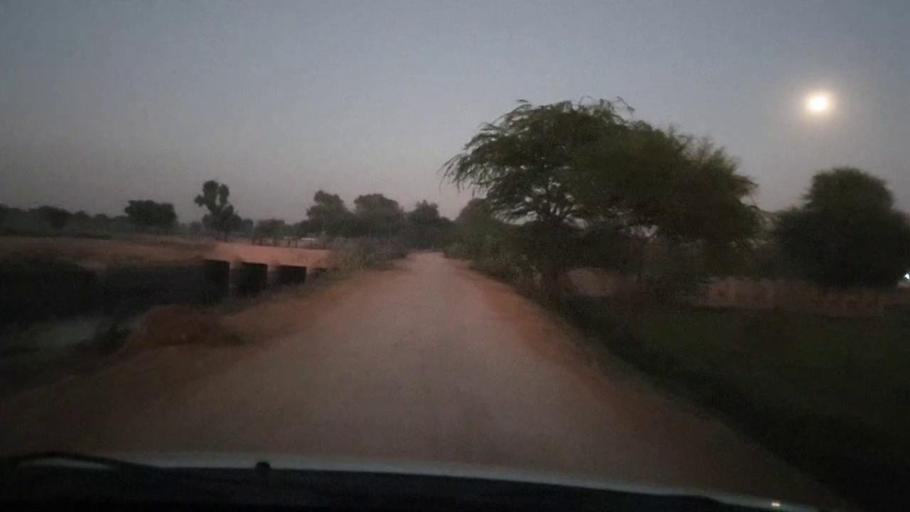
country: PK
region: Sindh
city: Khairpur Nathan Shah
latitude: 27.1341
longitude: 67.7336
